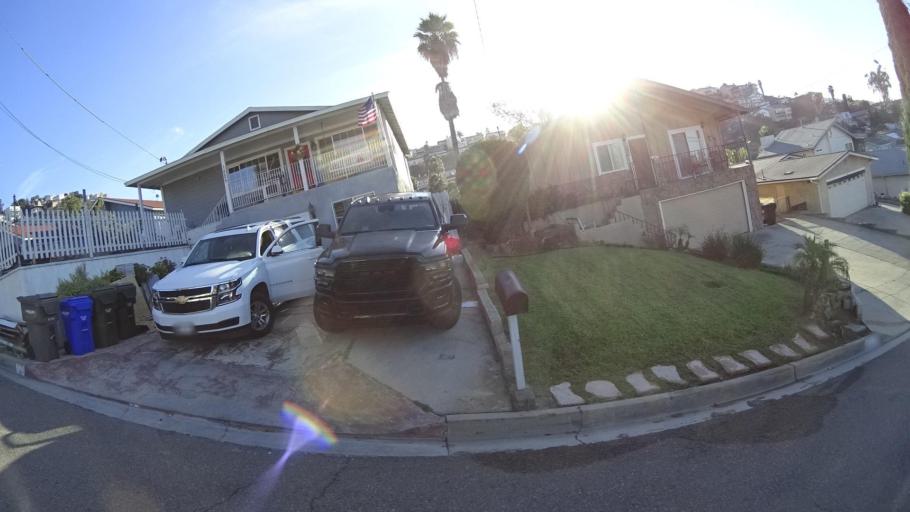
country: US
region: California
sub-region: San Diego County
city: La Presa
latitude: 32.7173
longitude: -116.9903
